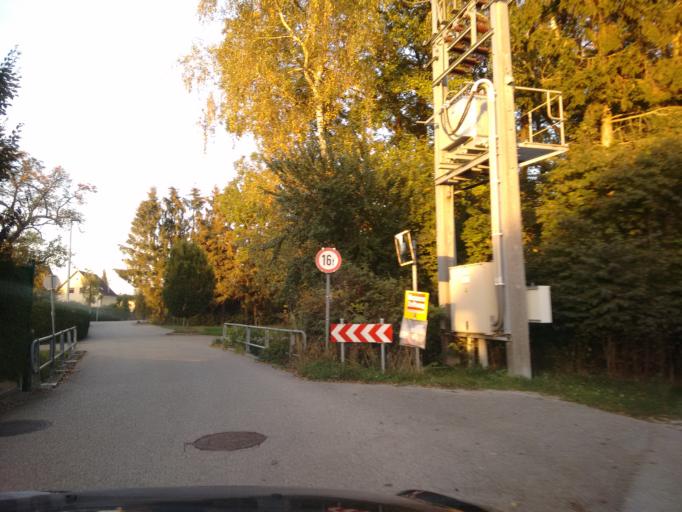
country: AT
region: Upper Austria
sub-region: Wels-Land
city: Gunskirchen
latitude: 48.1505
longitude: 13.9658
